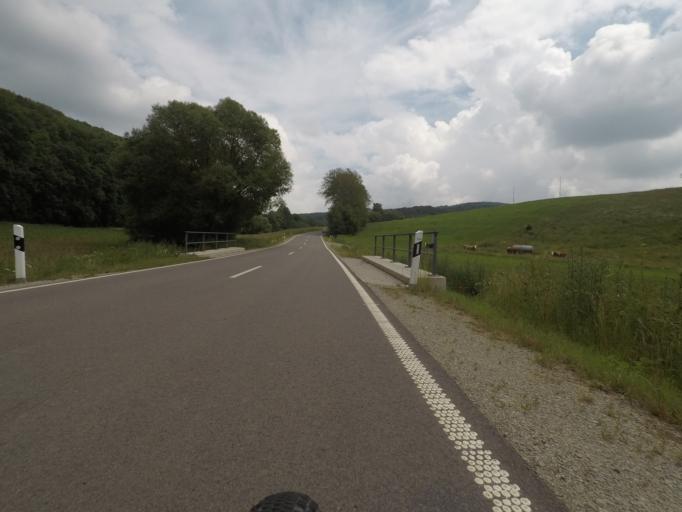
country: DE
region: Hesse
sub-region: Regierungsbezirk Kassel
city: Grossalmerode
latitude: 51.2071
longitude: 9.8124
